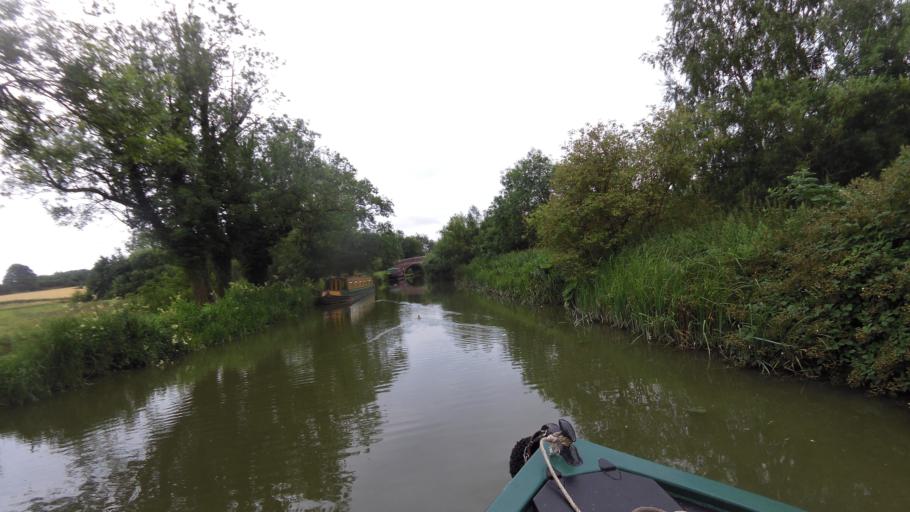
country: GB
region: England
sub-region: Wiltshire
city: Great Bedwyn
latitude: 51.3726
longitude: -1.6043
